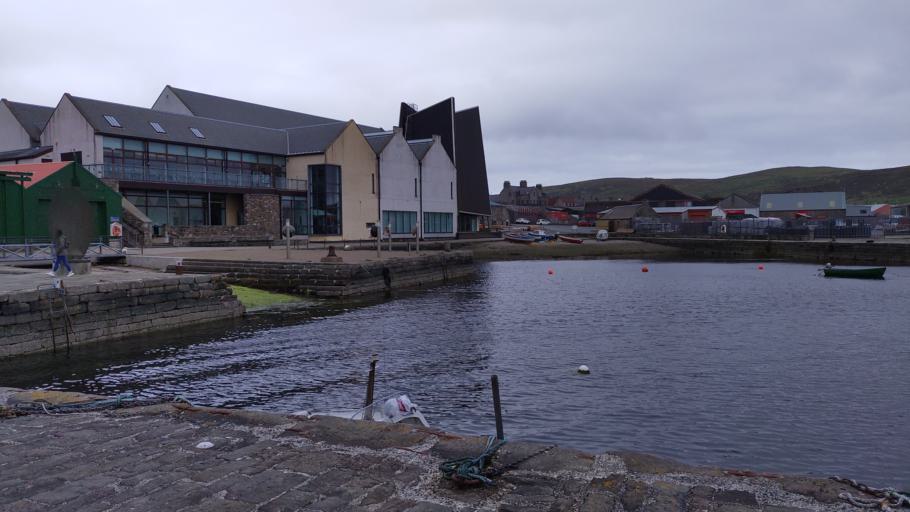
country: GB
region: Scotland
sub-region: Shetland Islands
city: Shetland
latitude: 60.1584
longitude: -1.1490
